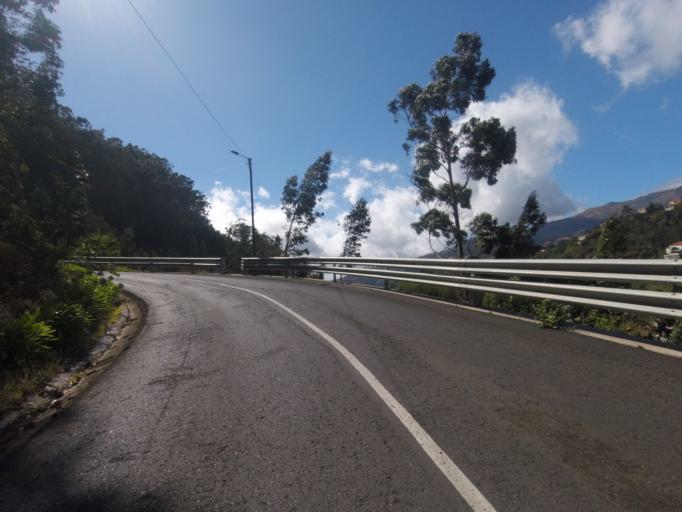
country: PT
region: Madeira
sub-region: Ribeira Brava
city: Campanario
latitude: 32.6875
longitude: -17.0303
